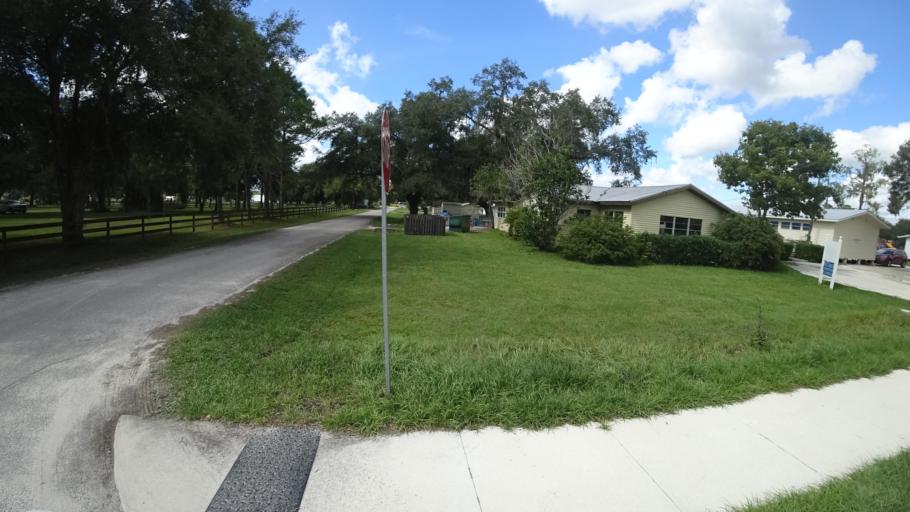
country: US
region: Florida
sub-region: Sarasota County
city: Lake Sarasota
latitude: 27.3492
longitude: -82.1605
